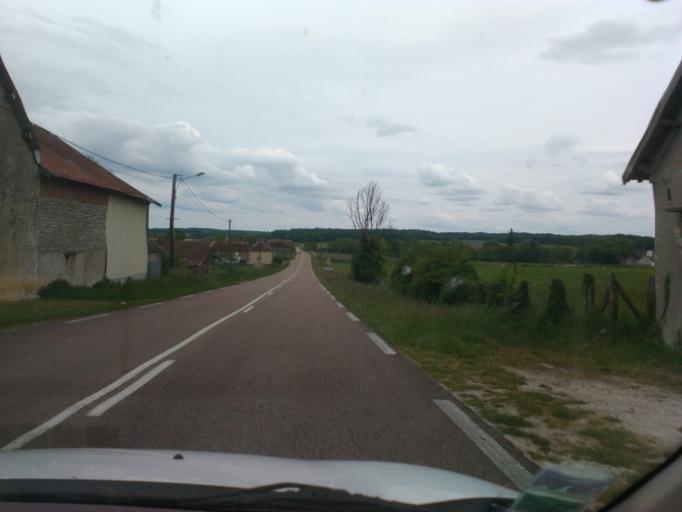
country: FR
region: Champagne-Ardenne
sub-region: Departement de l'Aube
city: Vendeuvre-sur-Barse
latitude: 48.2361
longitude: 4.3899
